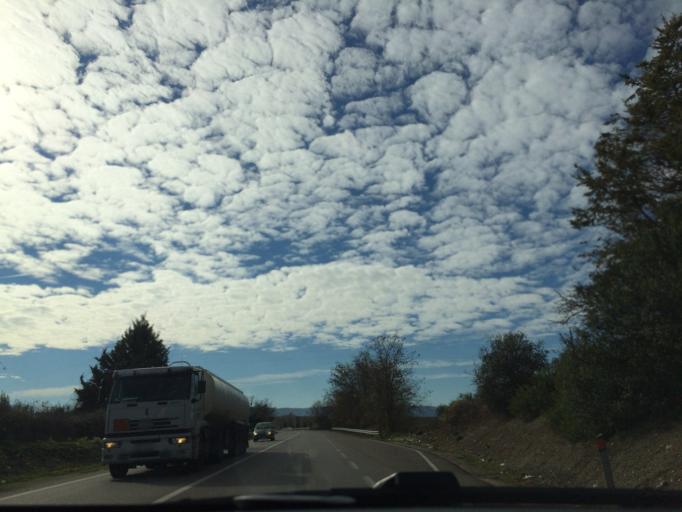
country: IT
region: Basilicate
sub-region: Provincia di Matera
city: La Martella
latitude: 40.6053
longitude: 16.5688
